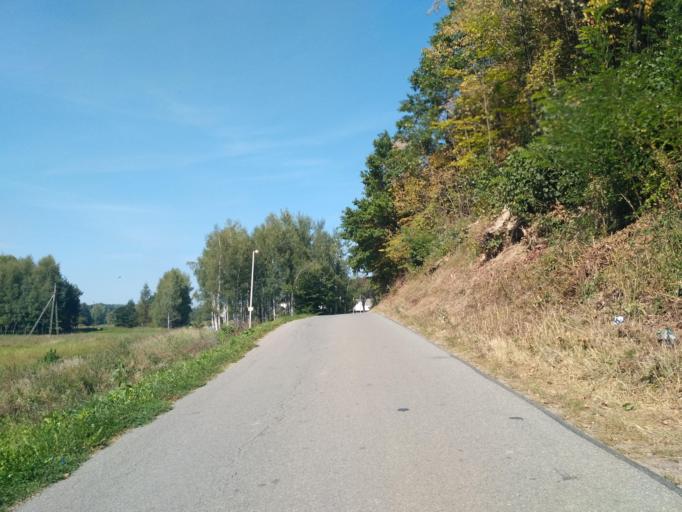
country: PL
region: Subcarpathian Voivodeship
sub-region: Powiat brzozowski
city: Grabownica Starzenska
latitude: 49.6453
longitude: 22.0989
